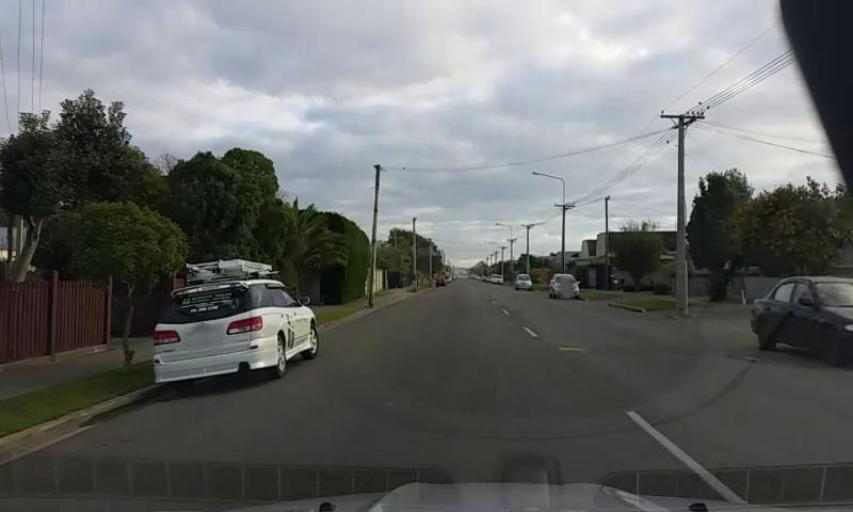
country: NZ
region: Canterbury
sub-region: Christchurch City
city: Christchurch
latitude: -43.5299
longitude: 172.7355
